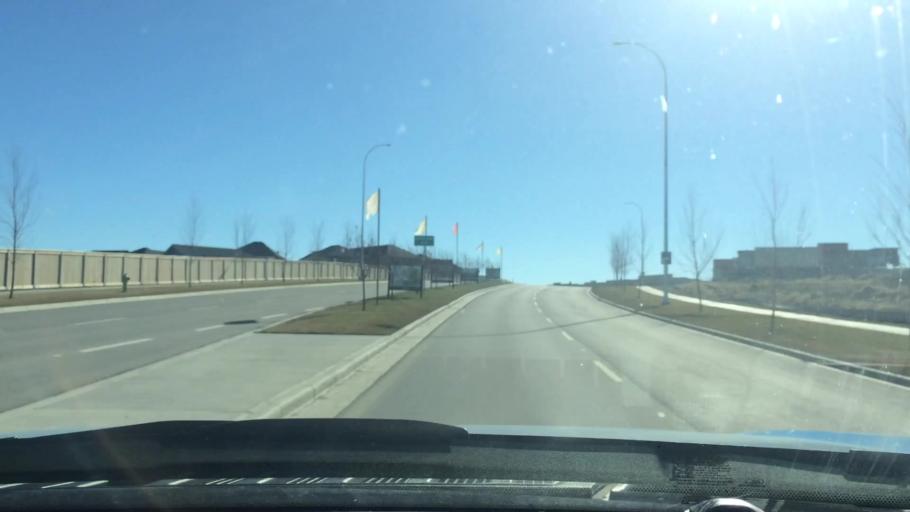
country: CA
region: Alberta
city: Calgary
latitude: 51.1646
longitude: -114.1602
